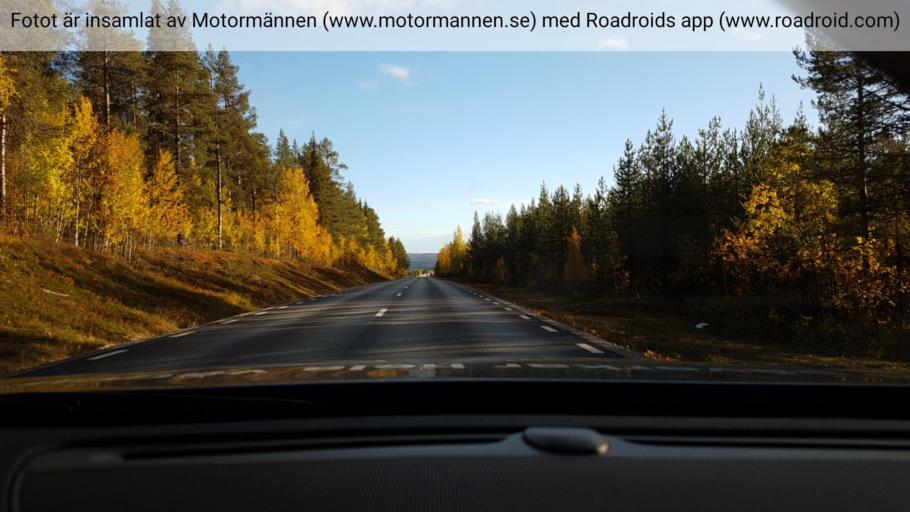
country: SE
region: Norrbotten
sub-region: Jokkmokks Kommun
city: Jokkmokk
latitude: 66.8969
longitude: 19.8272
